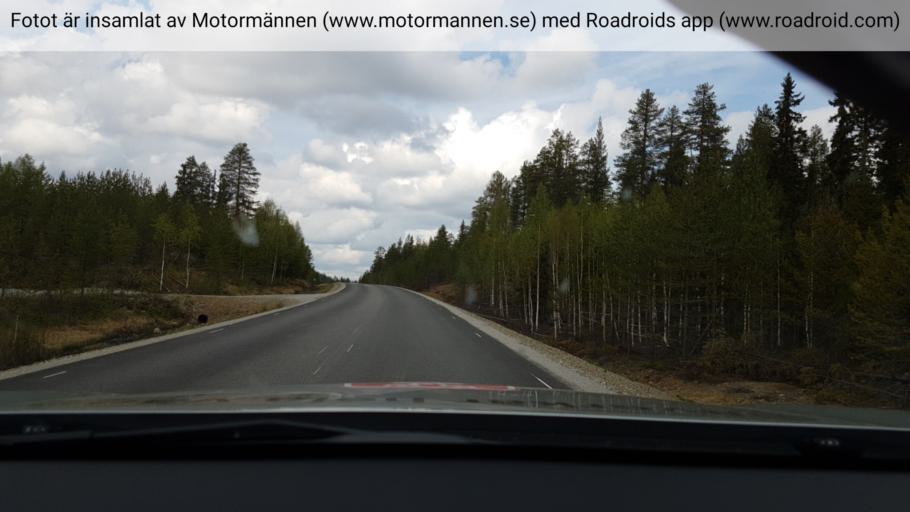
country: SE
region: Vaesterbotten
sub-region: Lycksele Kommun
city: Lycksele
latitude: 64.0233
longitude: 18.4494
